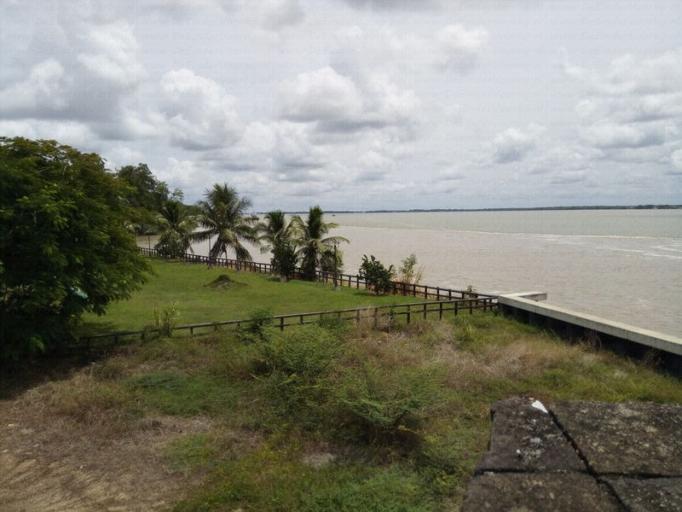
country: SR
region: Paramaribo
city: Paramaribo
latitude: 5.8250
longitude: -55.1496
